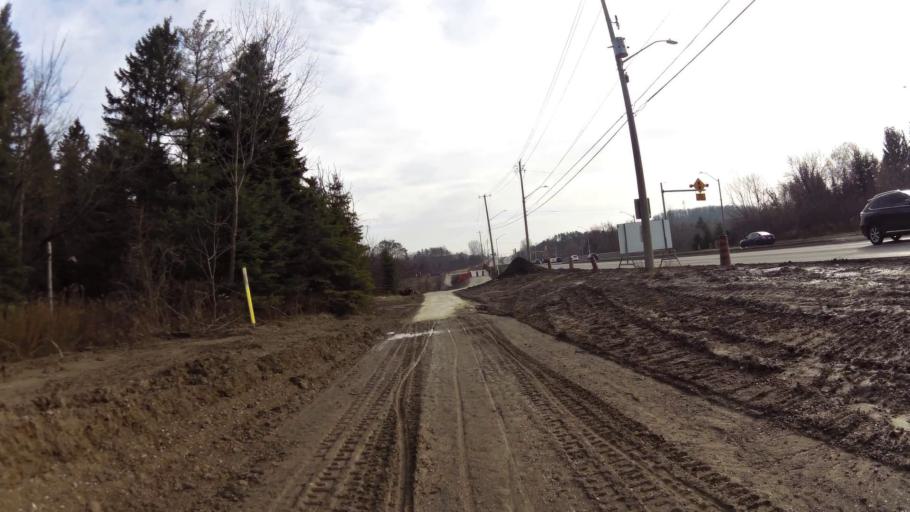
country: CA
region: Ontario
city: Kitchener
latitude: 43.3905
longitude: -80.4240
